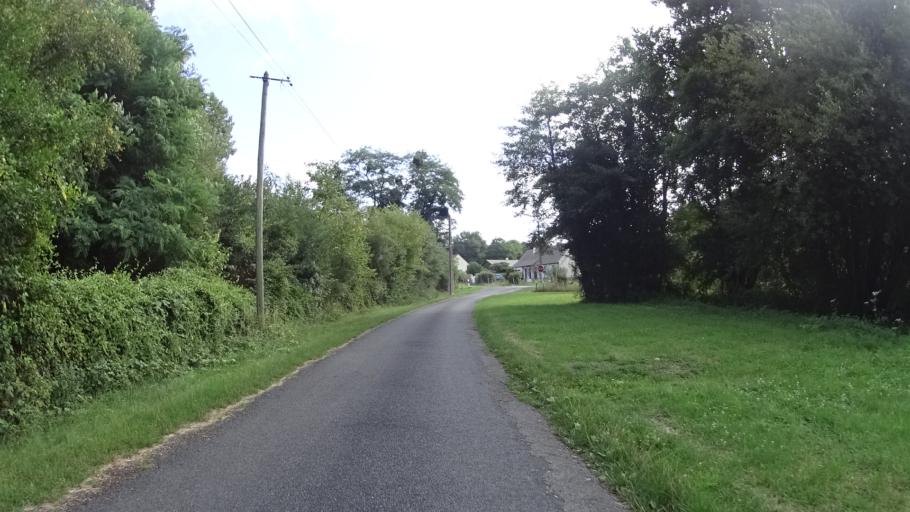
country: FR
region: Centre
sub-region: Departement du Loiret
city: Bouzy-la-Foret
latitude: 47.8767
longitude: 2.4402
